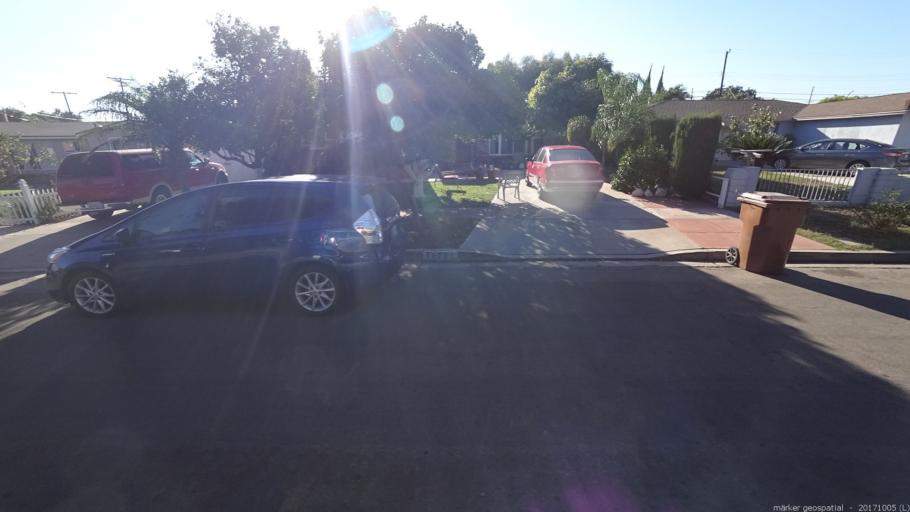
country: US
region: California
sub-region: Orange County
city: Stanton
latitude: 33.7924
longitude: -117.9822
